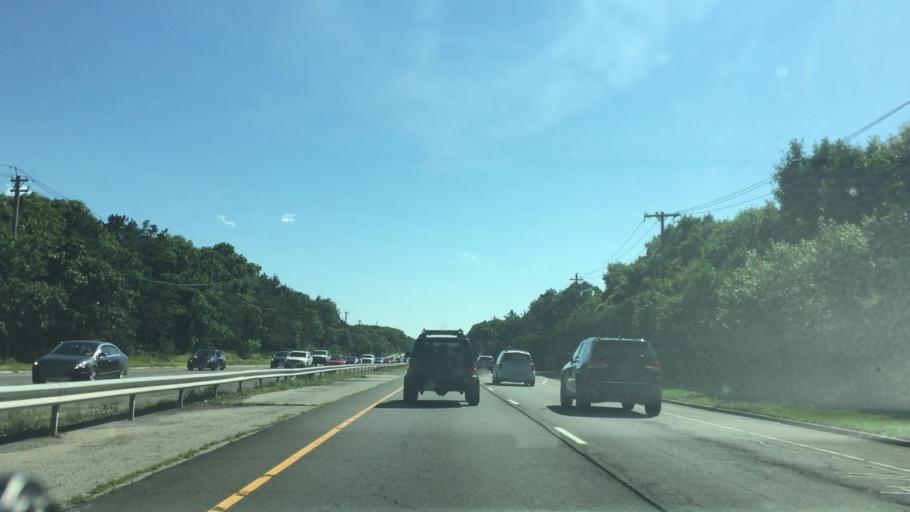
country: US
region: New York
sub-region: Suffolk County
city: Terryville
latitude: 40.8929
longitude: -73.0909
